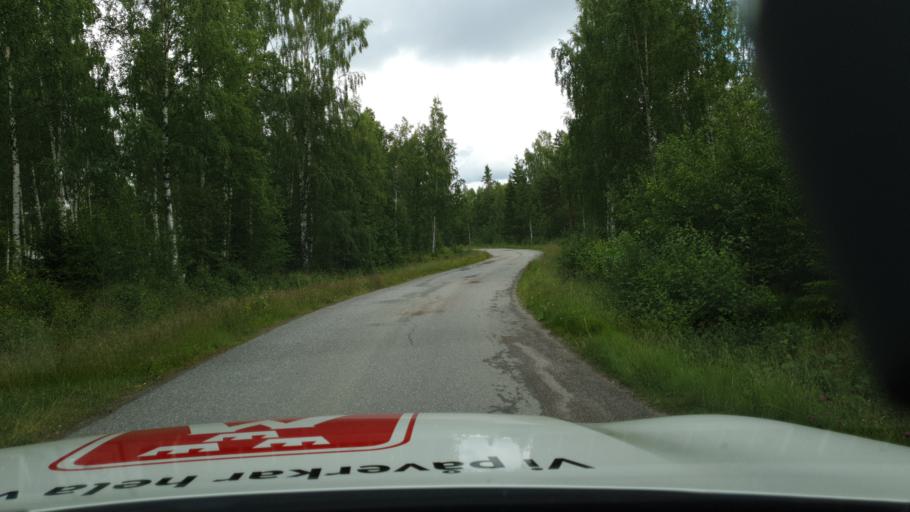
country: SE
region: Vaesterbotten
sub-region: Umea Kommun
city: Hoernefors
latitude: 63.6146
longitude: 19.9997
